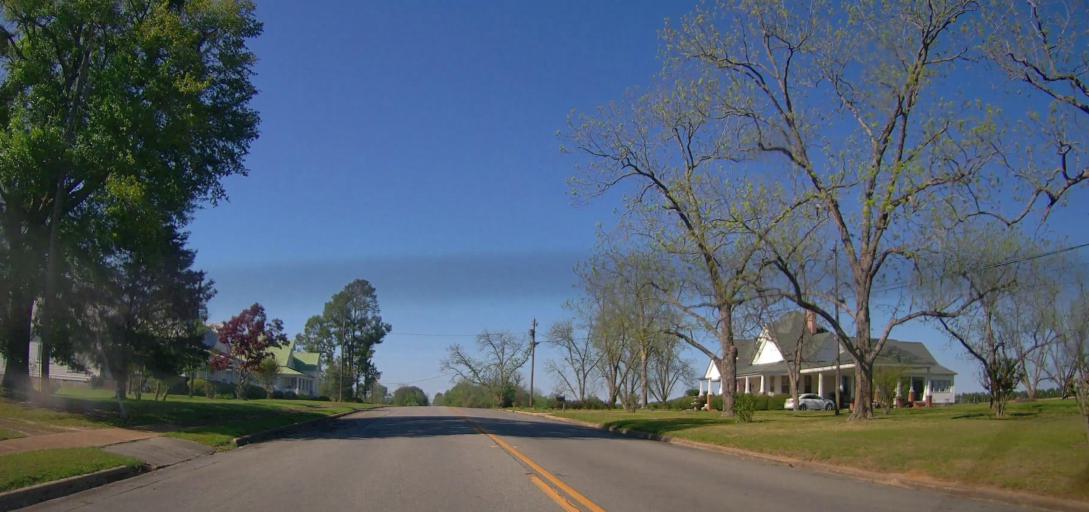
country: US
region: Georgia
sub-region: Wilcox County
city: Rochelle
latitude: 31.9588
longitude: -83.4563
